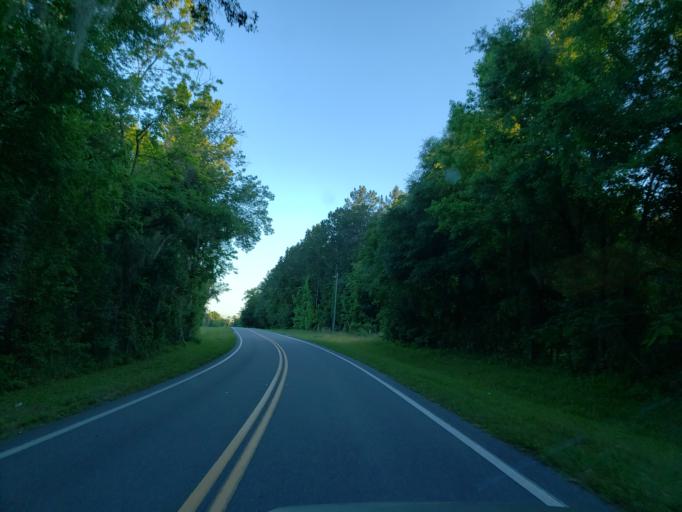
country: US
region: Florida
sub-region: Madison County
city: Madison
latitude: 30.6146
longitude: -83.2556
